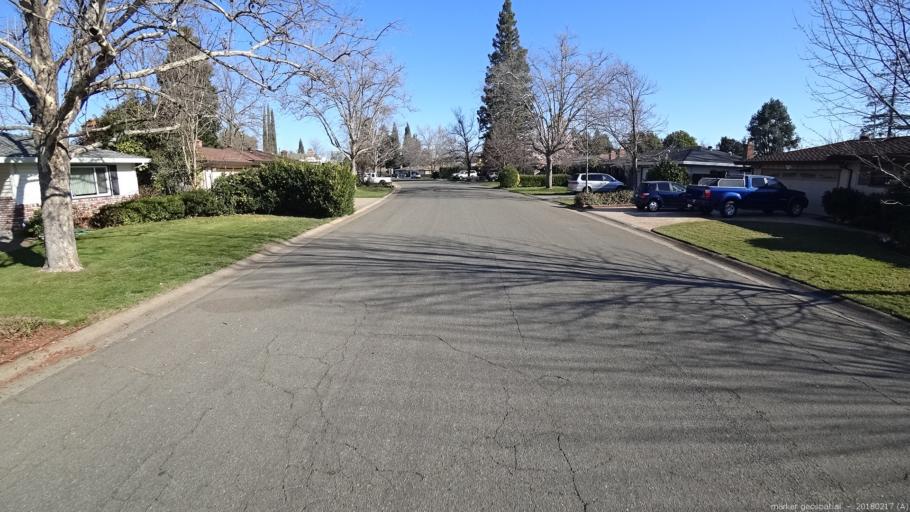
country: US
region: California
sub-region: Sacramento County
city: Folsom
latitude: 38.6614
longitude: -121.1956
